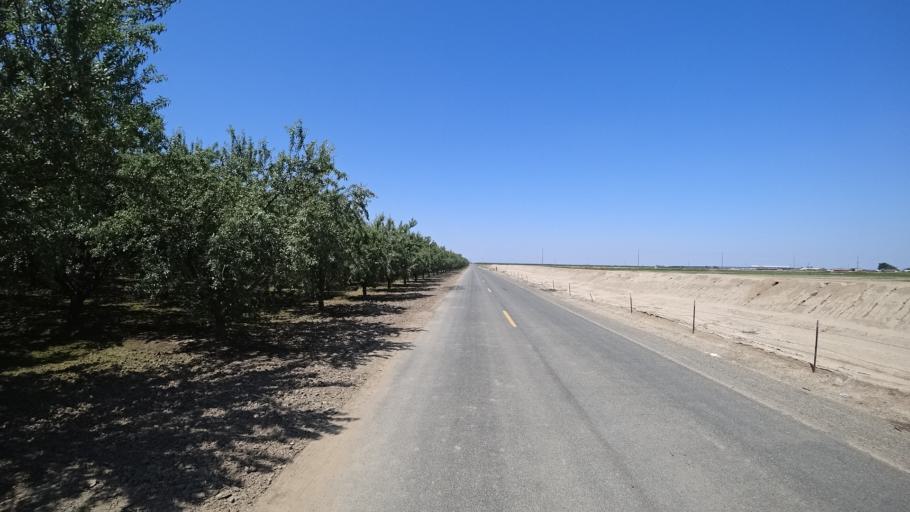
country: US
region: California
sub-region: Kings County
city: Home Garden
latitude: 36.2840
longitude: -119.5796
